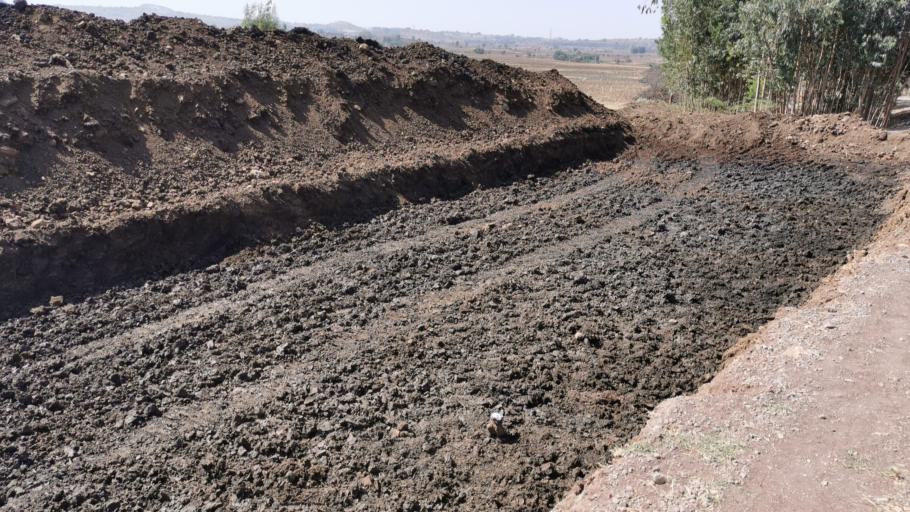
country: ET
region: Amhara
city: Bahir Dar
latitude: 11.8429
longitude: 37.0023
